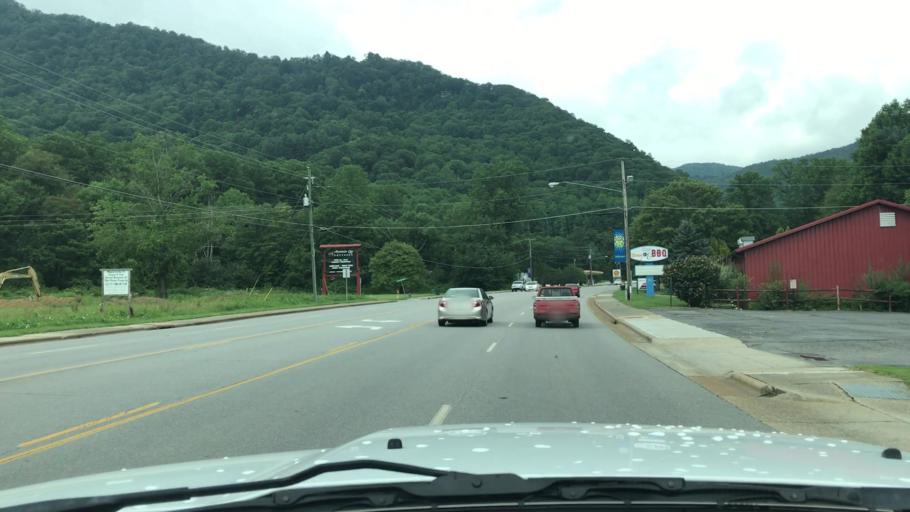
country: US
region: North Carolina
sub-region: Haywood County
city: Maggie Valley
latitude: 35.5183
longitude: -83.1017
